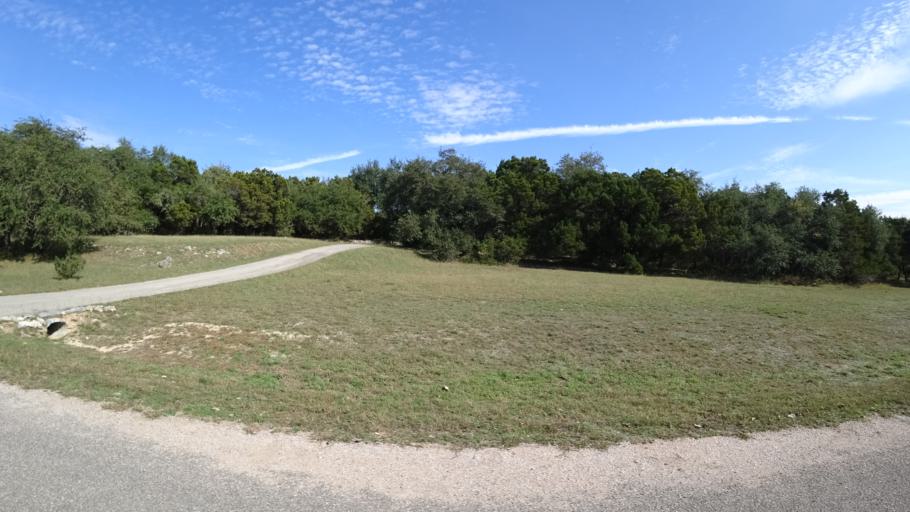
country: US
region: Texas
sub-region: Travis County
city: Barton Creek
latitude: 30.2275
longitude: -97.9184
